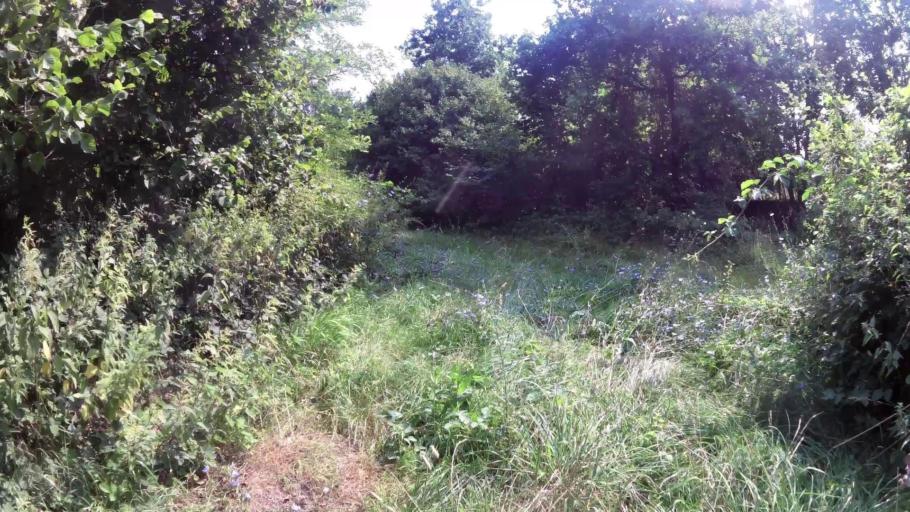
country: PL
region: West Pomeranian Voivodeship
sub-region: Powiat gryfinski
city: Chojna
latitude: 52.9039
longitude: 14.5120
